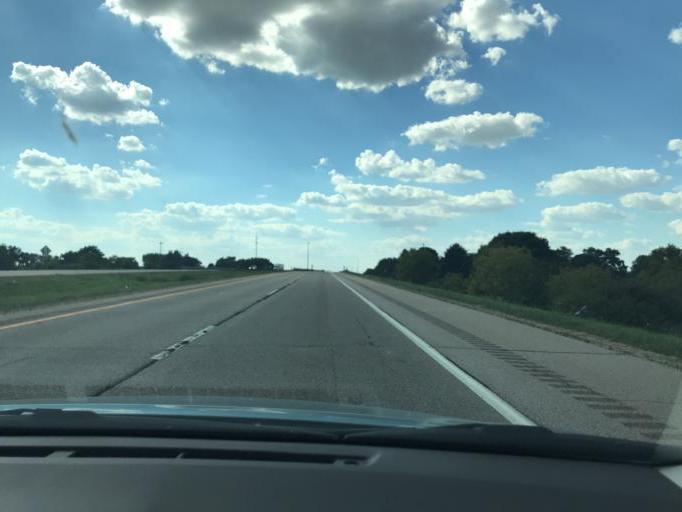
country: US
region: Wisconsin
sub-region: Rock County
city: Clinton
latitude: 42.5728
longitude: -88.8612
